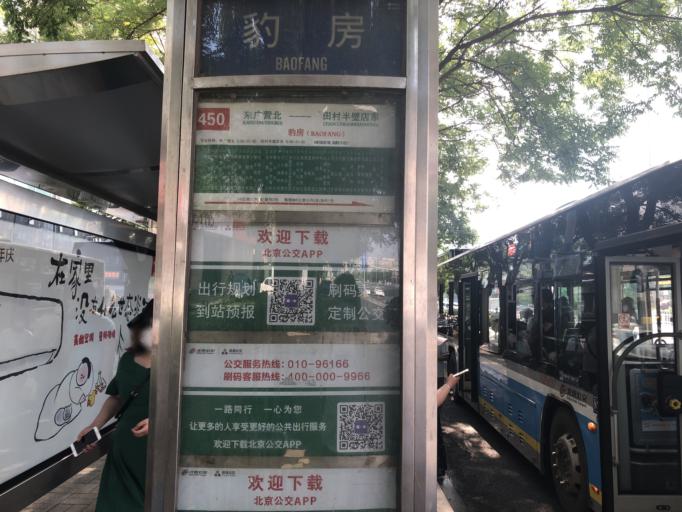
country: CN
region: Beijing
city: Datun
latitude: 40.0013
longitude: 116.3990
